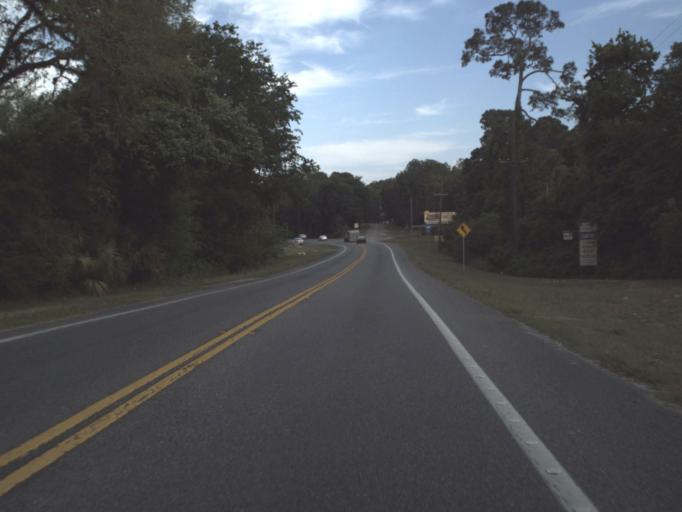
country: US
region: Florida
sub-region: Marion County
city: Silver Springs Shores
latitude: 29.1994
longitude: -81.9309
